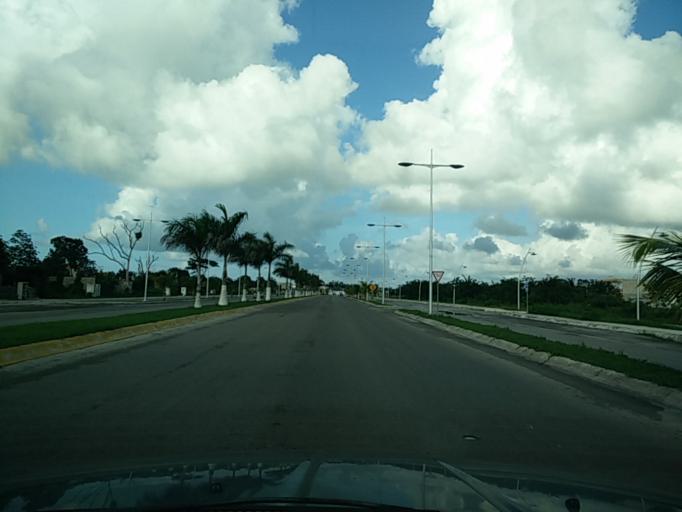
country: MX
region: Quintana Roo
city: San Miguel de Cozumel
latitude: 20.4895
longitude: -86.9348
